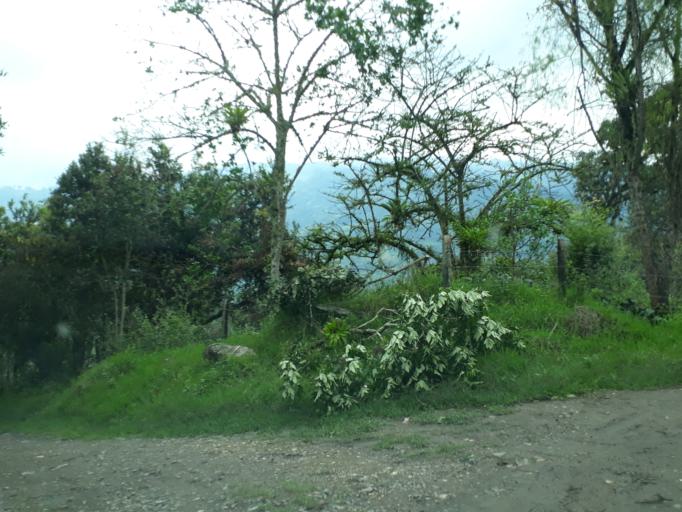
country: CO
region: Cundinamarca
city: Manta
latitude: 4.9901
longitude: -73.5628
